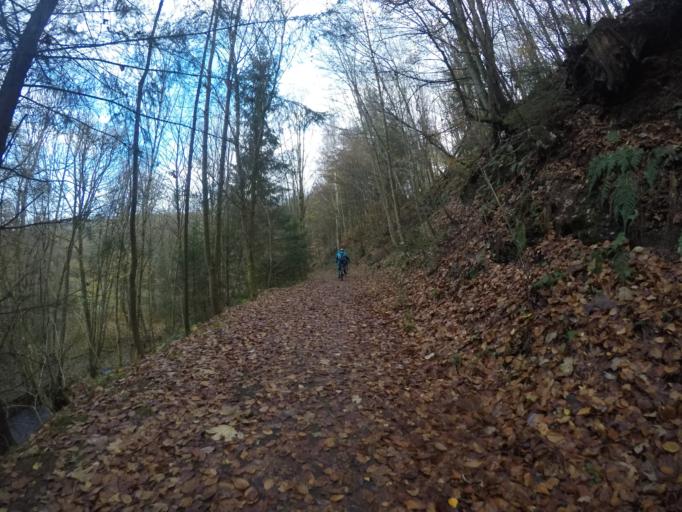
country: BE
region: Wallonia
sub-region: Province du Luxembourg
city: Habay-la-Vieille
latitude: 49.7265
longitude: 5.6272
